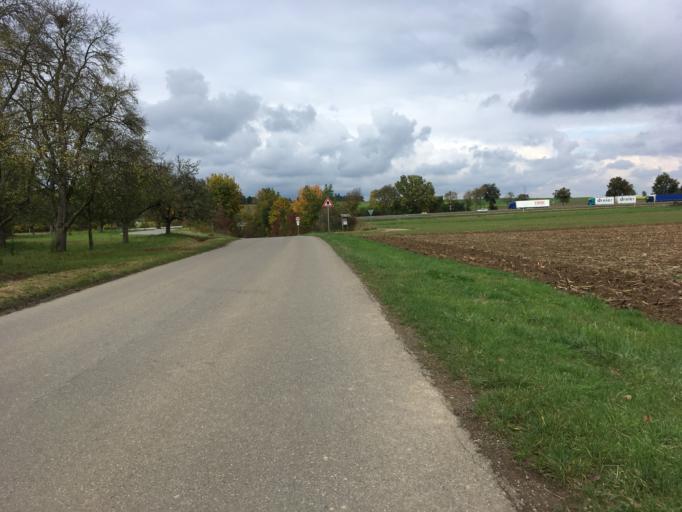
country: DE
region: Baden-Wuerttemberg
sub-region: Tuebingen Region
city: Kusterdingen
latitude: 48.5054
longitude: 9.1022
